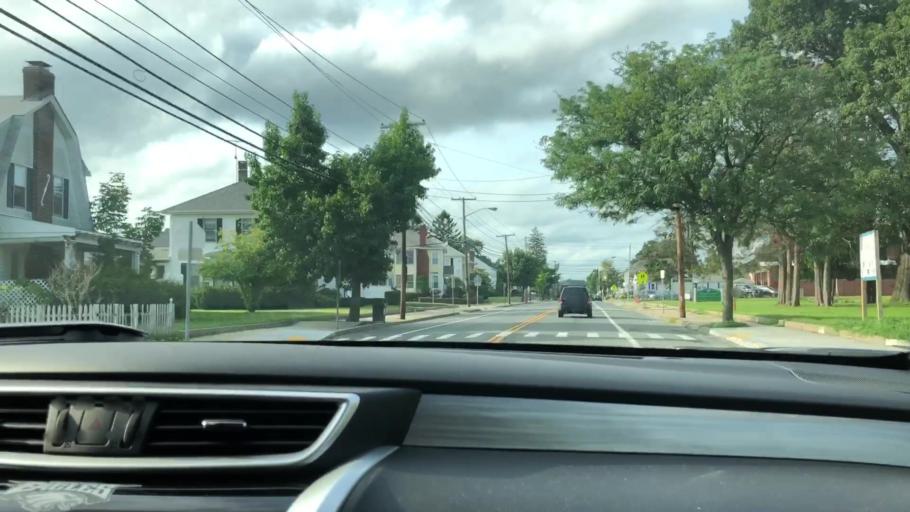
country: US
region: Rhode Island
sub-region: Providence County
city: Central Falls
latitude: 41.8672
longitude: -71.4129
